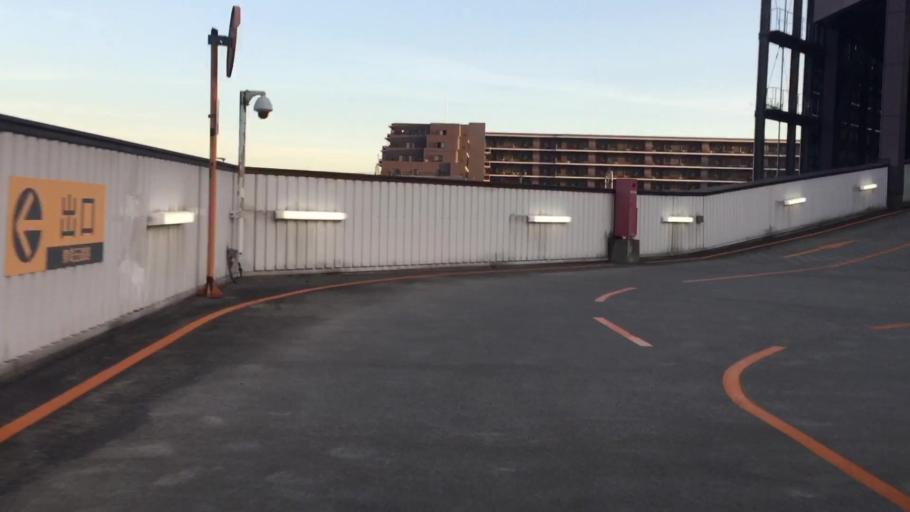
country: JP
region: Saitama
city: Yoshikawa
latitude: 35.8776
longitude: 139.8266
